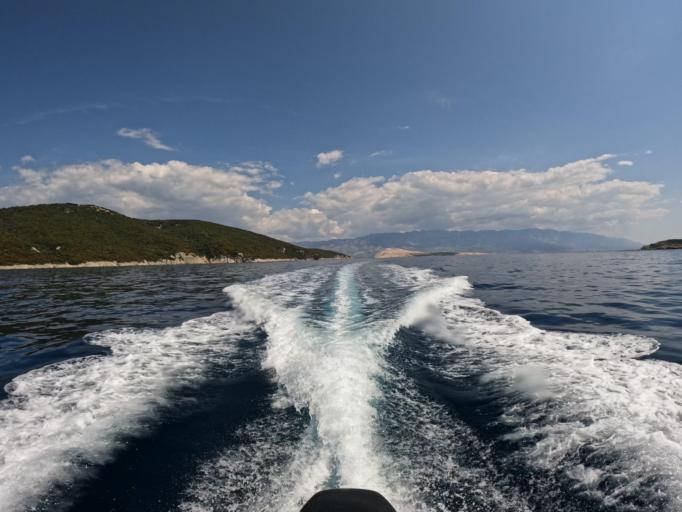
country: HR
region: Primorsko-Goranska
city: Lopar
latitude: 44.8549
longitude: 14.7473
